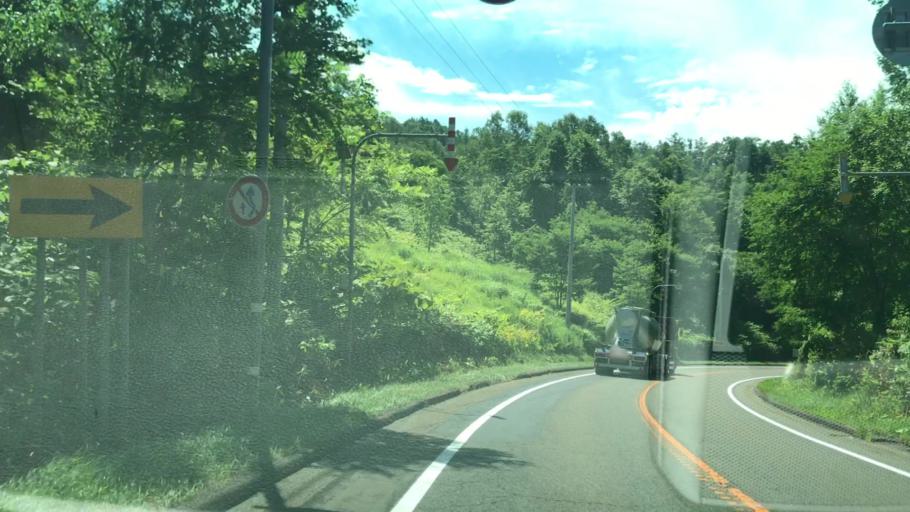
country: JP
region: Hokkaido
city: Shimo-furano
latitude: 42.9021
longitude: 142.4384
